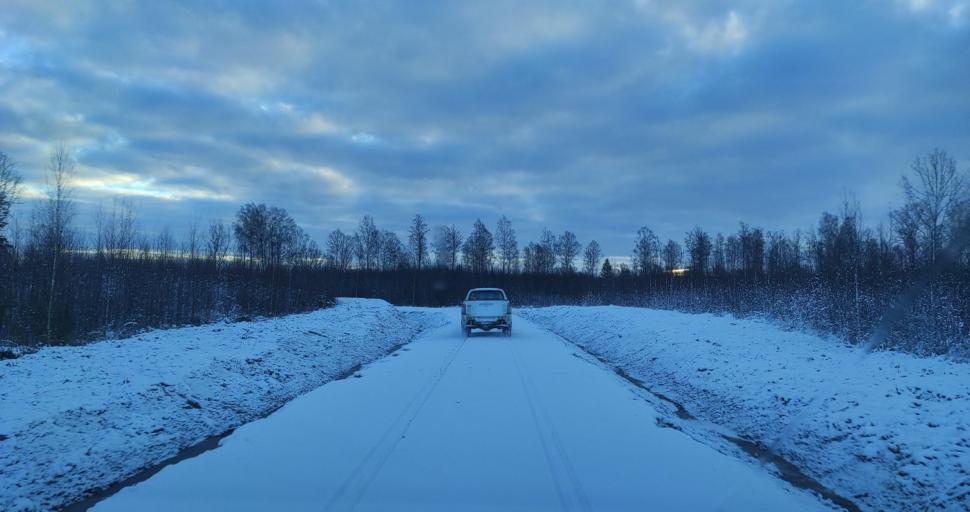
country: LV
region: Skrunda
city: Skrunda
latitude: 56.5842
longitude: 21.9415
